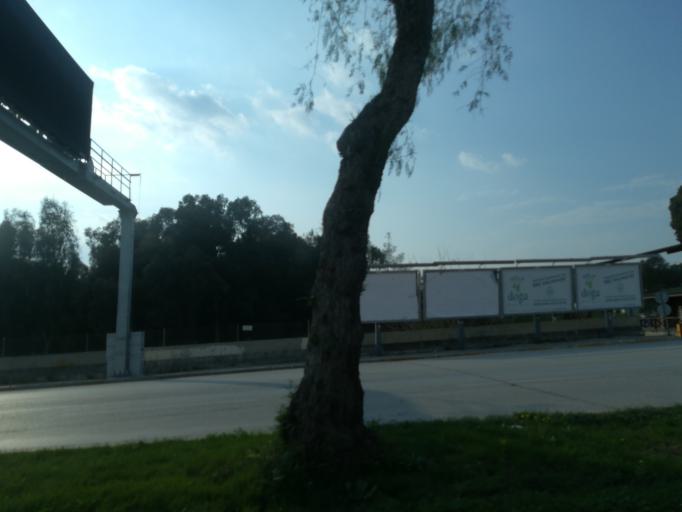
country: TR
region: Adana
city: Adana
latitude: 37.0278
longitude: 35.3448
